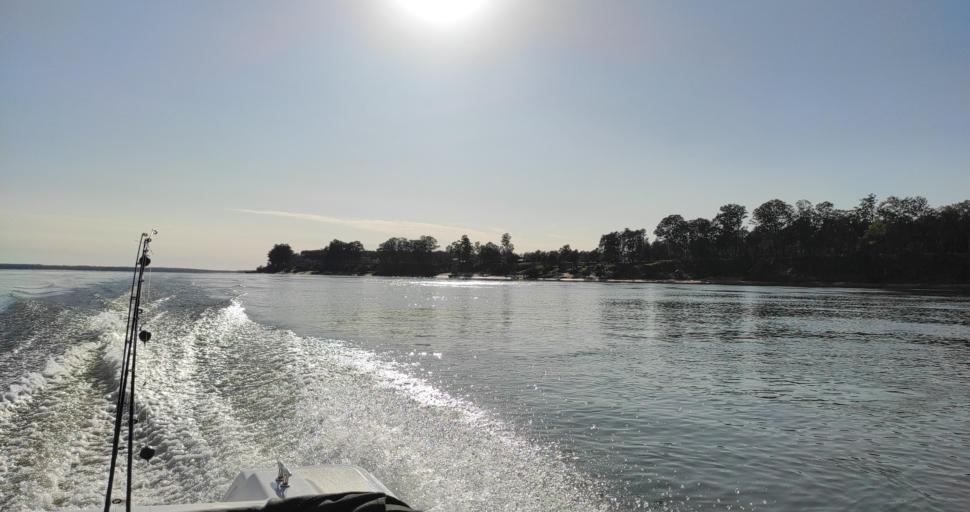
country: AR
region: Corrientes
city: Ituzaingo
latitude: -27.6031
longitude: -56.8230
